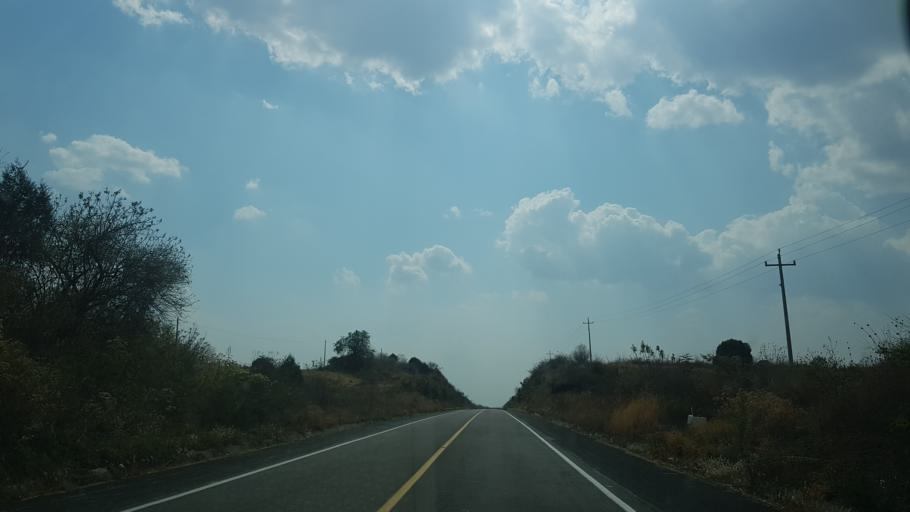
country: MX
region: Puebla
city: San Juan Amecac
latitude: 18.8162
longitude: -98.6648
